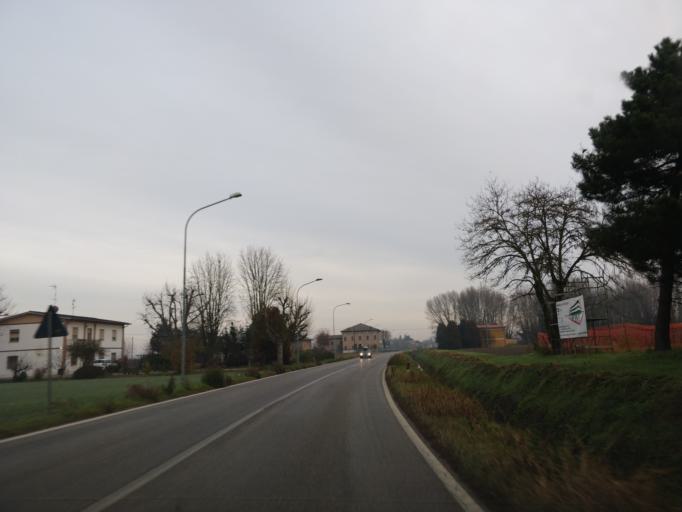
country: IT
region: Emilia-Romagna
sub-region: Provincia di Ferrara
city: Corpo Reno
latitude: 44.7643
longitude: 11.3191
